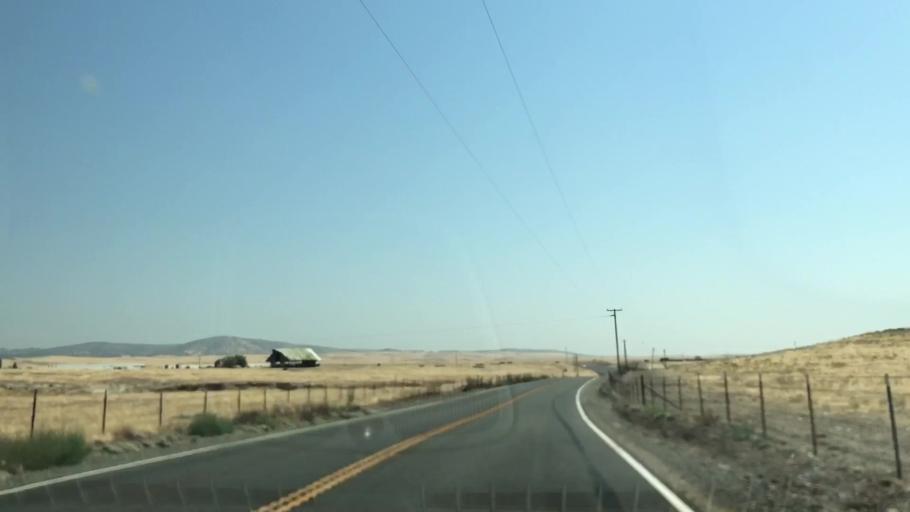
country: US
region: California
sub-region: Stanislaus County
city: East Oakdale
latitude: 37.9402
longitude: -120.8167
